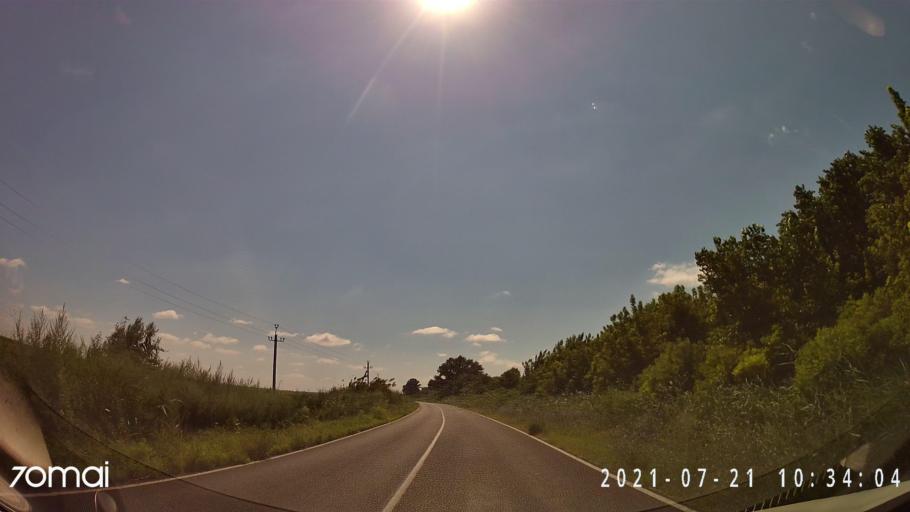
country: RO
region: Tulcea
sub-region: Oras Isaccea
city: Isaccea
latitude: 45.2970
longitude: 28.4404
